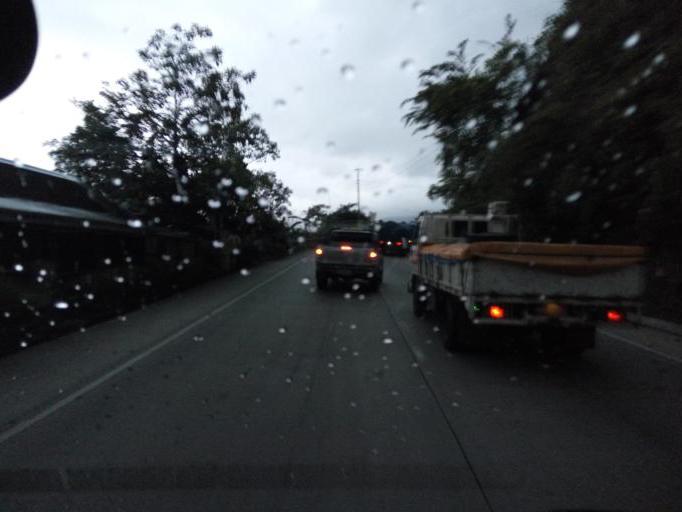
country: PH
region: Cagayan Valley
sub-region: Province of Nueva Vizcaya
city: Santa Fe
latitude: 16.1330
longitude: 120.9328
